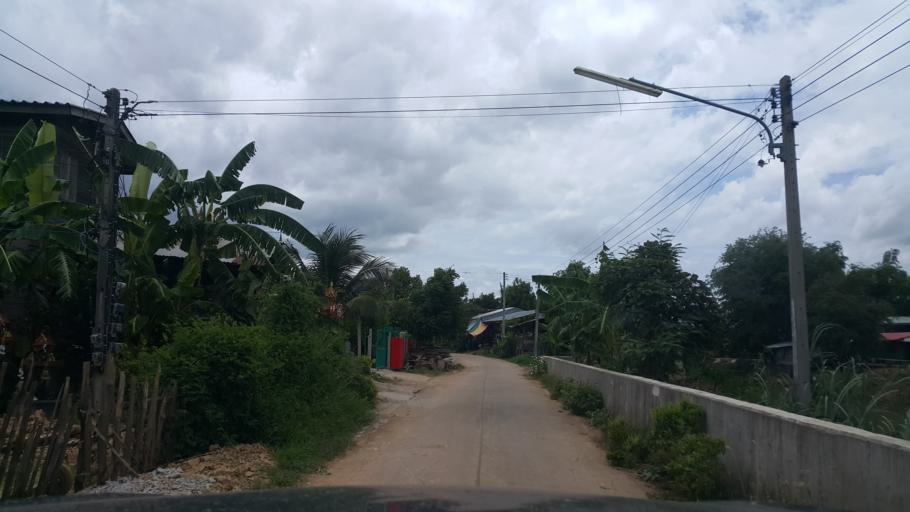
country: TH
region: Sukhothai
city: Sukhothai
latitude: 17.0226
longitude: 99.7956
